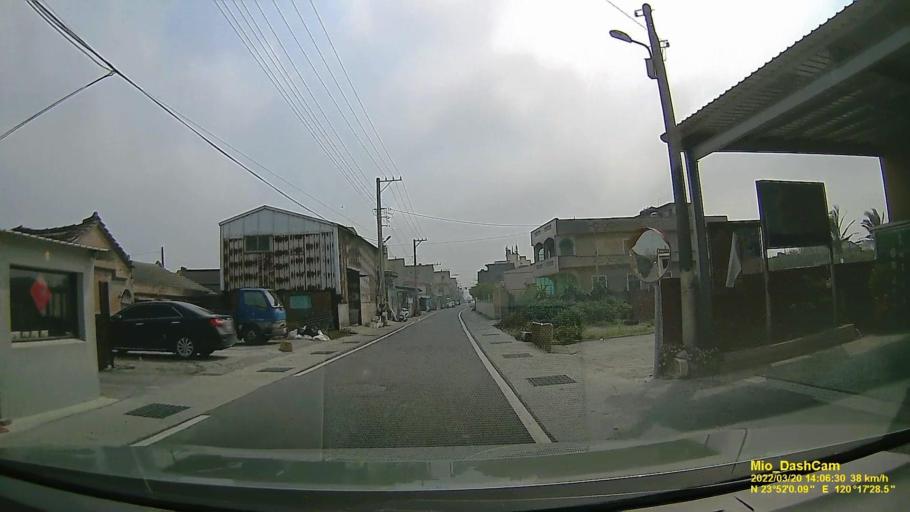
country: TW
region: Taiwan
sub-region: Yunlin
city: Douliu
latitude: 23.8666
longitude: 120.2912
